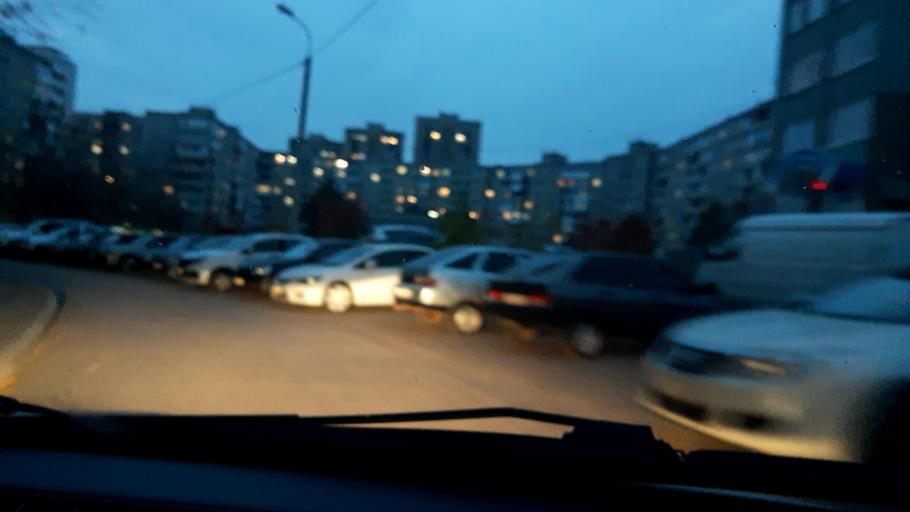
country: RU
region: Bashkortostan
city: Ufa
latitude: 54.7688
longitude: 56.0516
